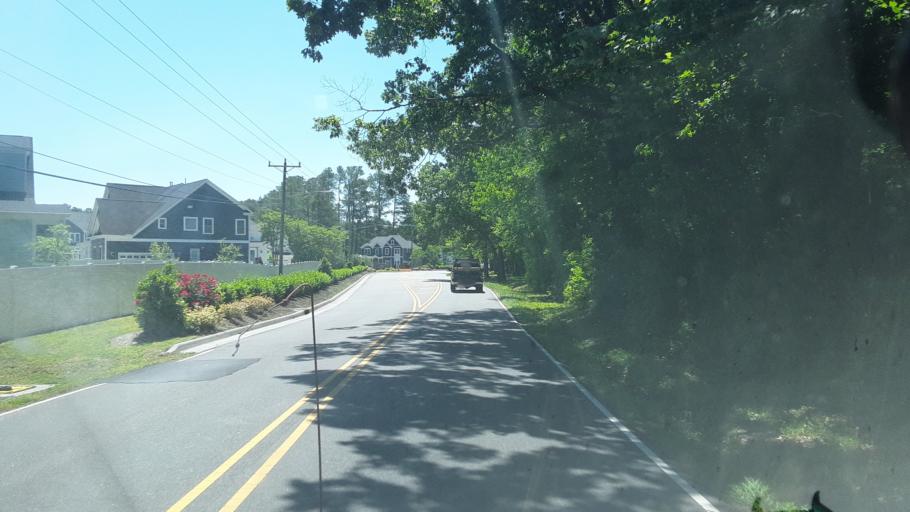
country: US
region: Virginia
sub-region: City of Virginia Beach
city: Virginia Beach
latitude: 36.7427
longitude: -75.9897
